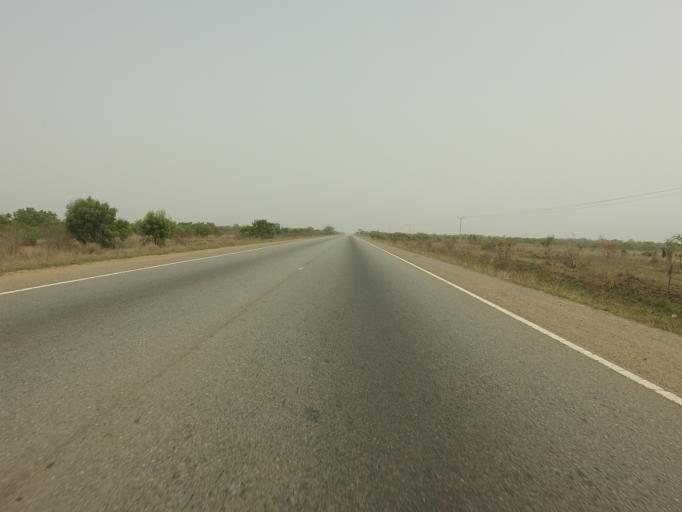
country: GH
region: Greater Accra
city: Tema
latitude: 5.8683
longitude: 0.3081
